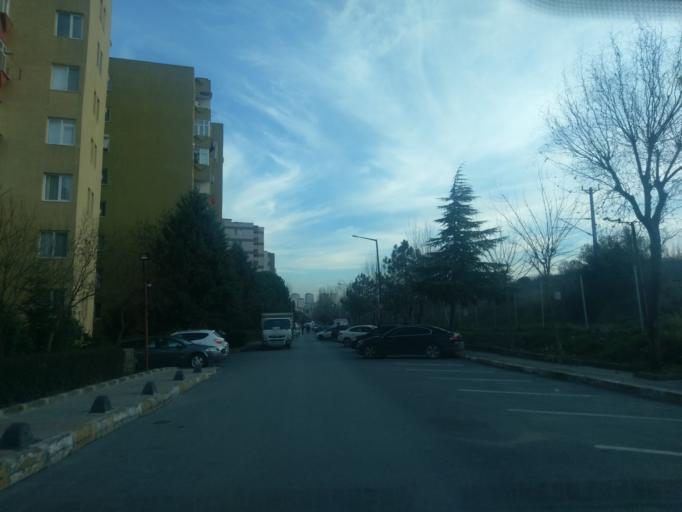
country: TR
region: Istanbul
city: Mahmutbey
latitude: 41.0374
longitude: 28.7620
